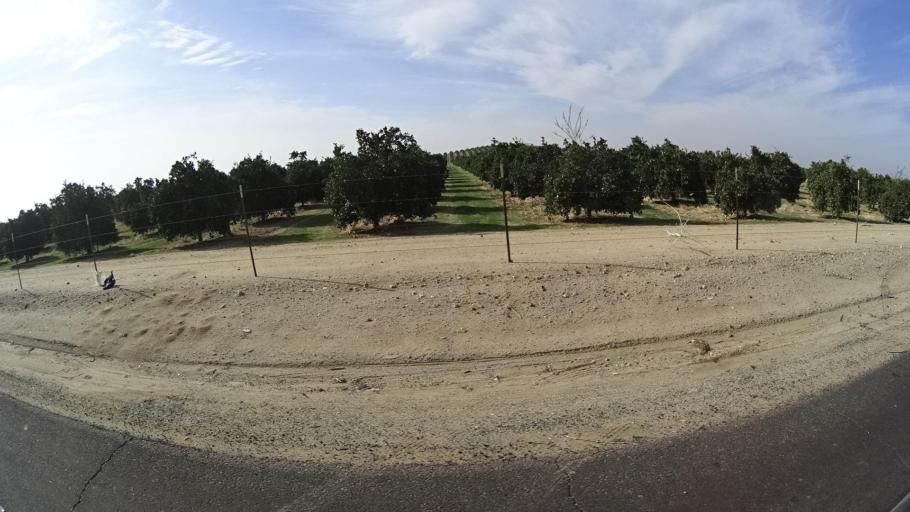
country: US
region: California
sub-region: Kern County
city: Lamont
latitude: 35.3500
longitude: -118.8432
